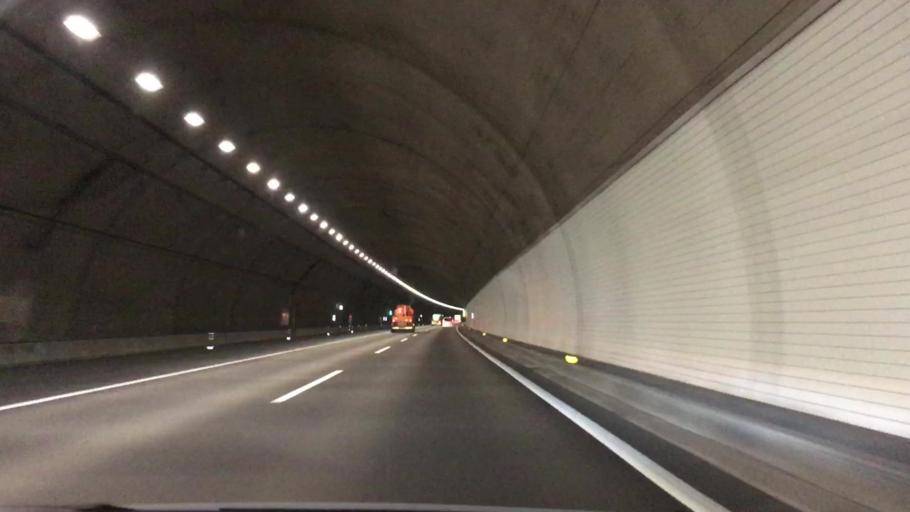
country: JP
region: Shizuoka
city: Hamakita
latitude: 34.8696
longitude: 137.6754
